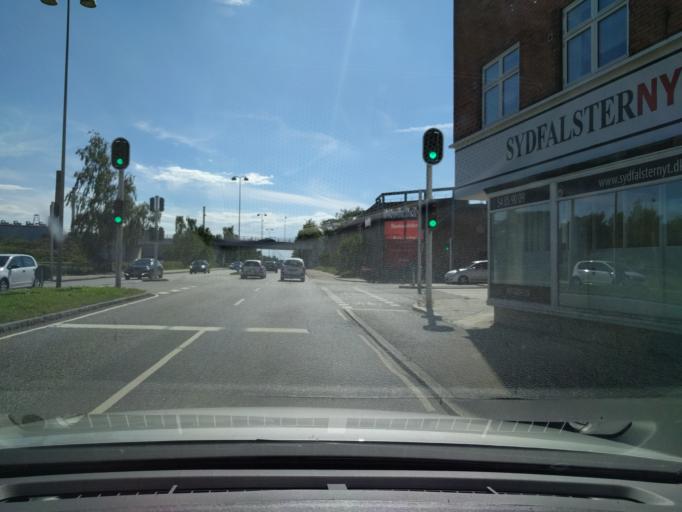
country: DK
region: Zealand
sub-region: Guldborgsund Kommune
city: Nykobing Falster
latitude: 54.7650
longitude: 11.8753
